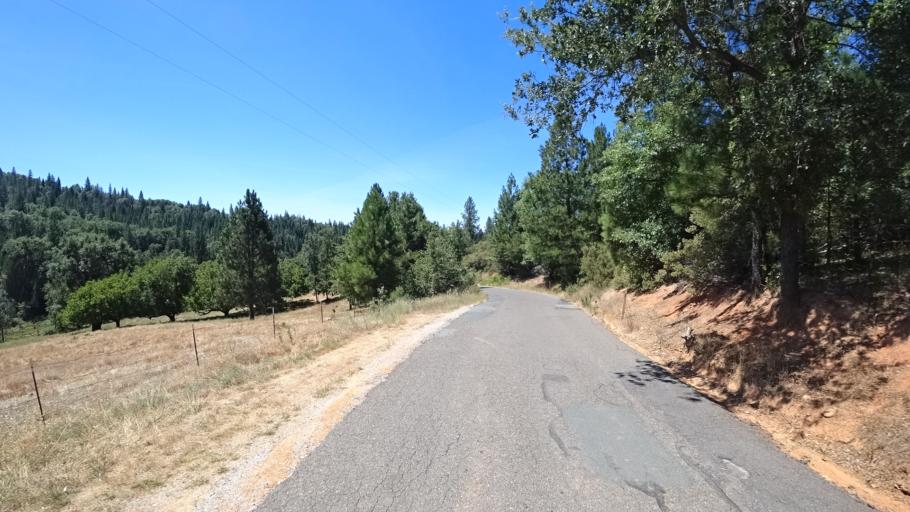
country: US
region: California
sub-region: Amador County
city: Pioneer
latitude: 38.4197
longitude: -120.5188
